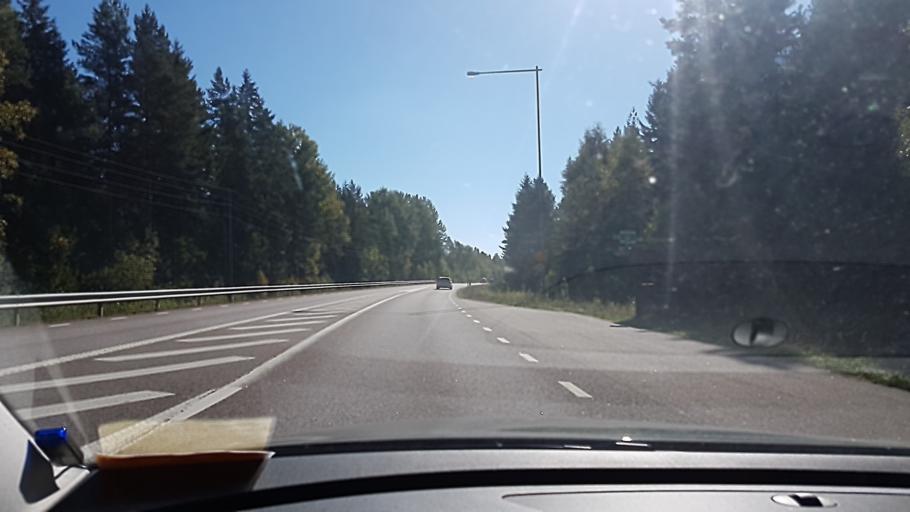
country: SE
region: Kronoberg
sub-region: Lessebo Kommun
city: Lessebo
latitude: 56.7793
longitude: 15.2471
